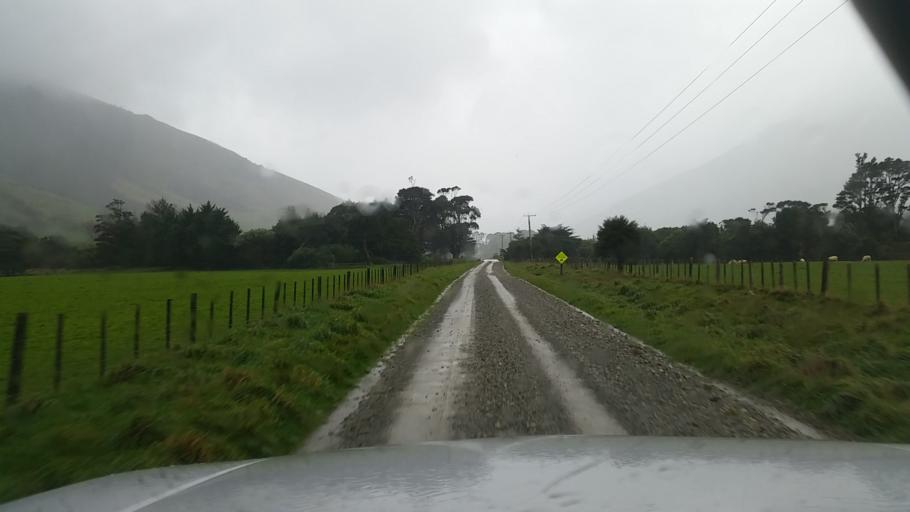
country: NZ
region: Marlborough
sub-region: Marlborough District
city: Picton
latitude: -41.1235
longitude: 174.0388
